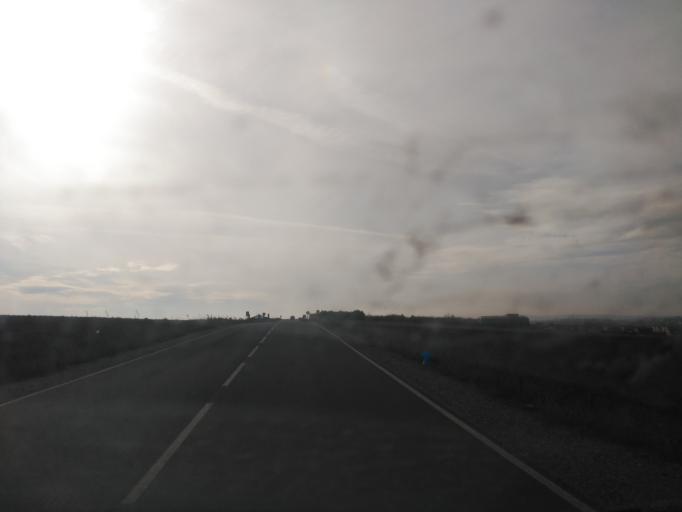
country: ES
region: Castille and Leon
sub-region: Provincia de Salamanca
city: Cabrerizos
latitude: 40.9858
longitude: -5.6028
